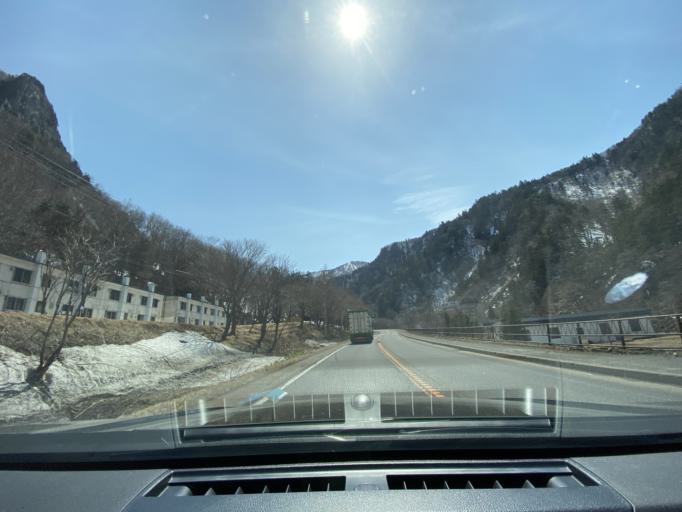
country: JP
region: Hokkaido
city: Kamikawa
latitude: 43.7335
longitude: 142.9424
